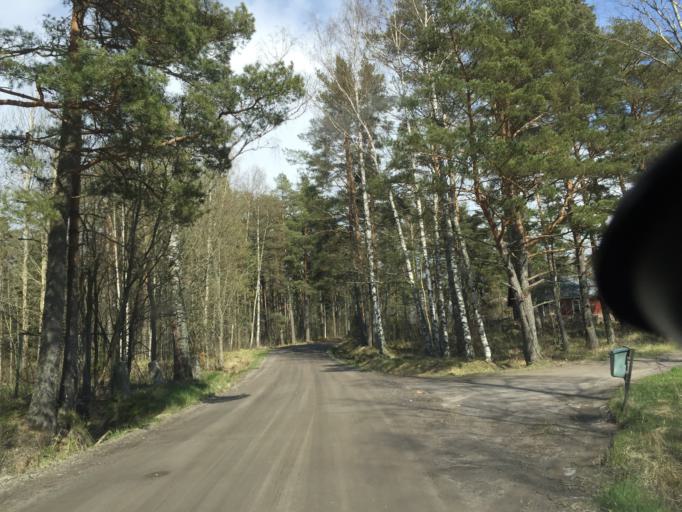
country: FI
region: Uusimaa
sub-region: Raaseporin
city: Hanko
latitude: 59.9400
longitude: 22.9122
